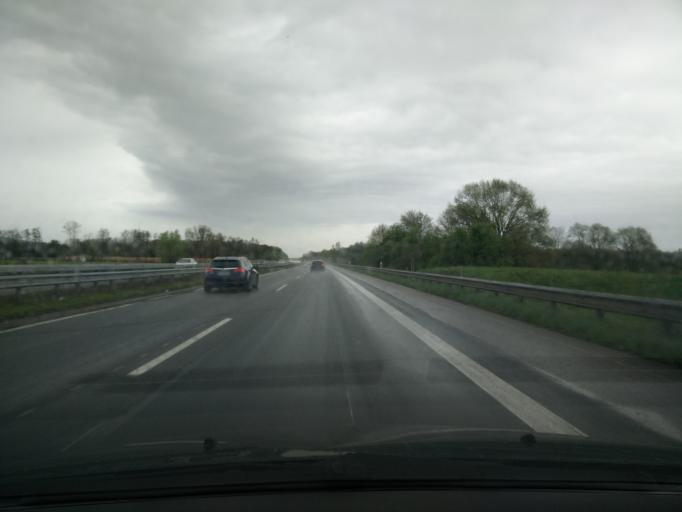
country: DE
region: Rheinland-Pfalz
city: Lachen-Speyerdorf
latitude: 49.3426
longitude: 8.1903
